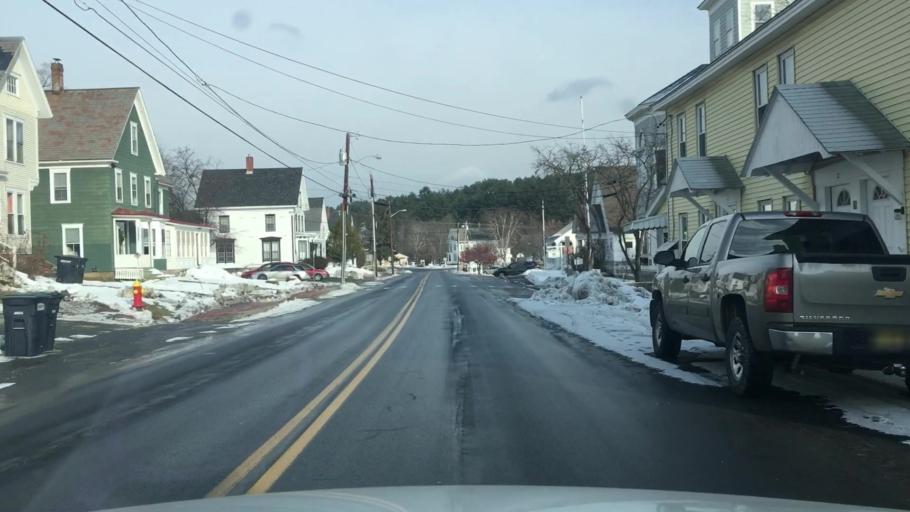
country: US
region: New Hampshire
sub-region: Grafton County
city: Enfield
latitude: 43.6426
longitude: -72.1445
